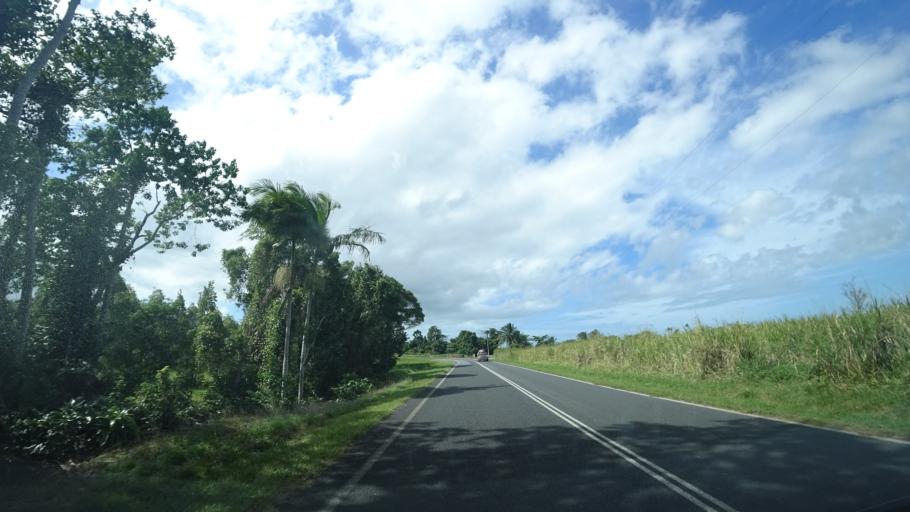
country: AU
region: Queensland
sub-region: Cairns
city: Port Douglas
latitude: -16.2777
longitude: 145.3852
